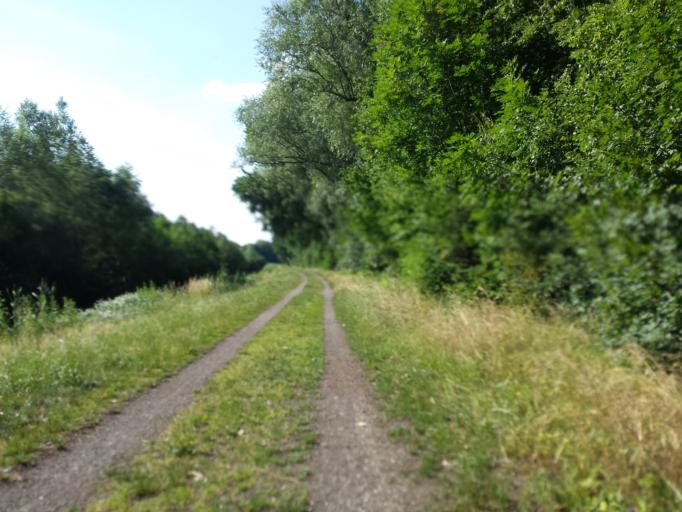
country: DE
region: Lower Saxony
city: Stuhr
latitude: 53.0885
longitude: 8.7482
